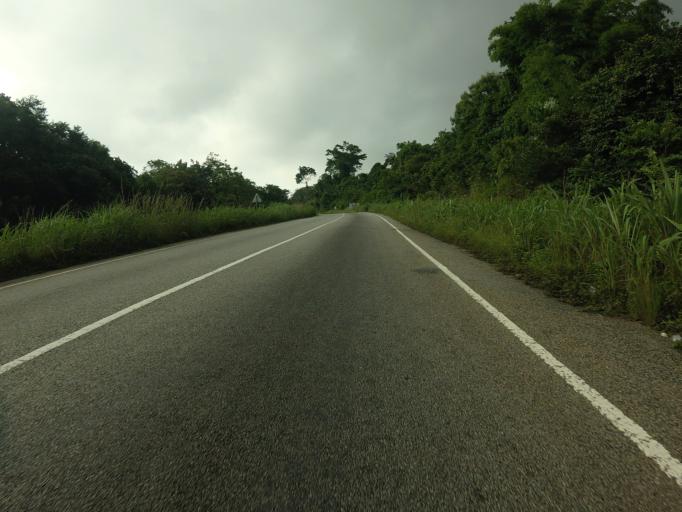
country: GH
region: Volta
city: Ho
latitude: 6.8129
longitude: 0.4207
